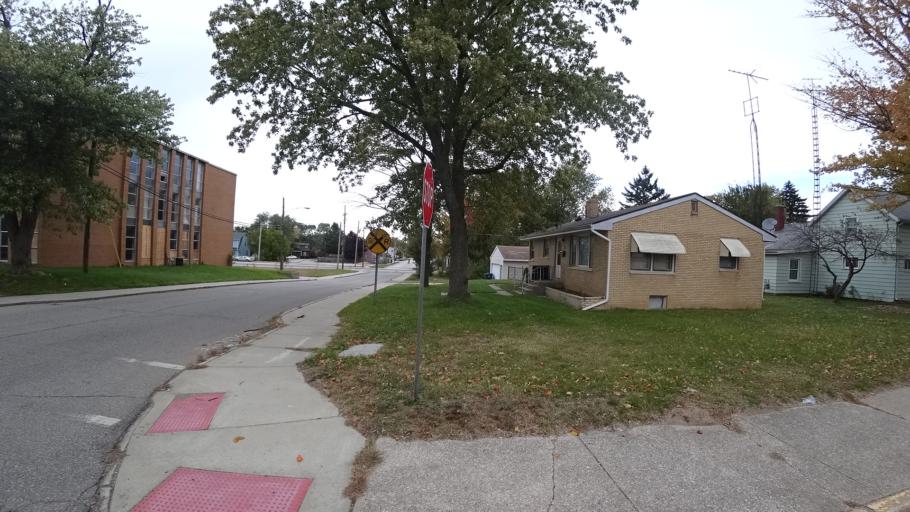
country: US
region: Indiana
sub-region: LaPorte County
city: Michigan City
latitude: 41.7122
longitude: -86.8936
